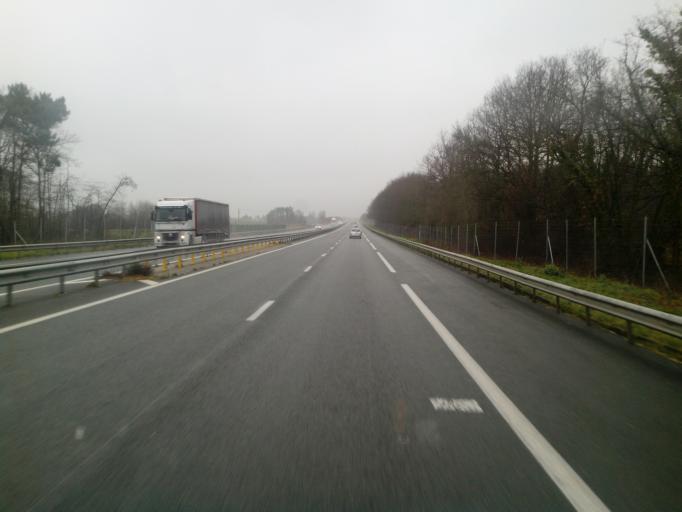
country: FR
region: Poitou-Charentes
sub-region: Departement de la Vienne
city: Savigny-Levescault
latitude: 46.4958
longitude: 0.4916
